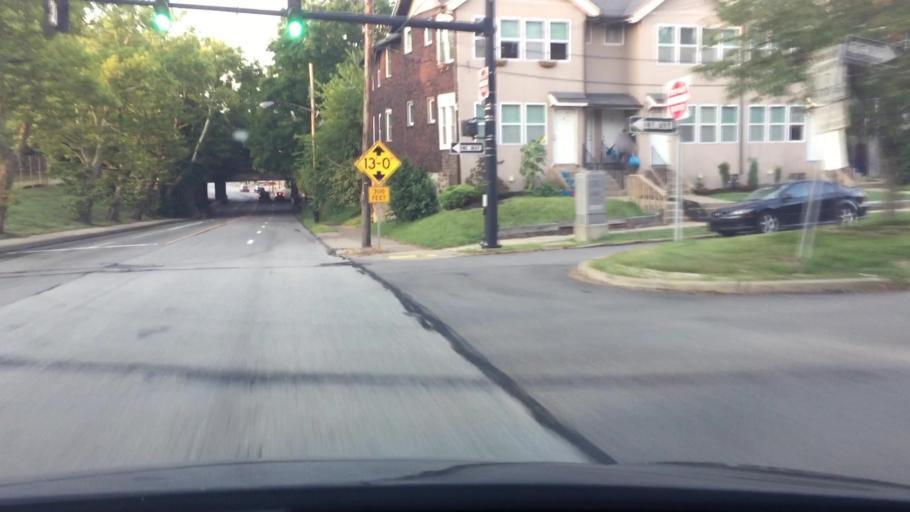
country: US
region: Pennsylvania
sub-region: Allegheny County
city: Wilkinsburg
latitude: 40.4556
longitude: -79.9106
